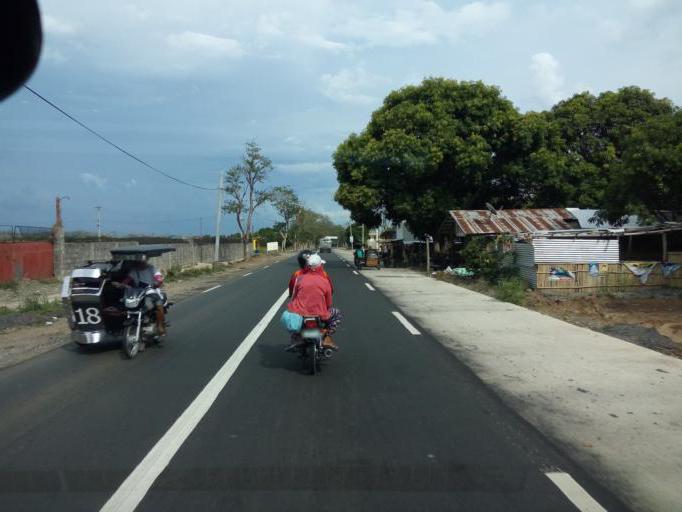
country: PH
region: Central Luzon
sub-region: Province of Nueva Ecija
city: Parista
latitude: 15.8258
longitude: 120.9507
